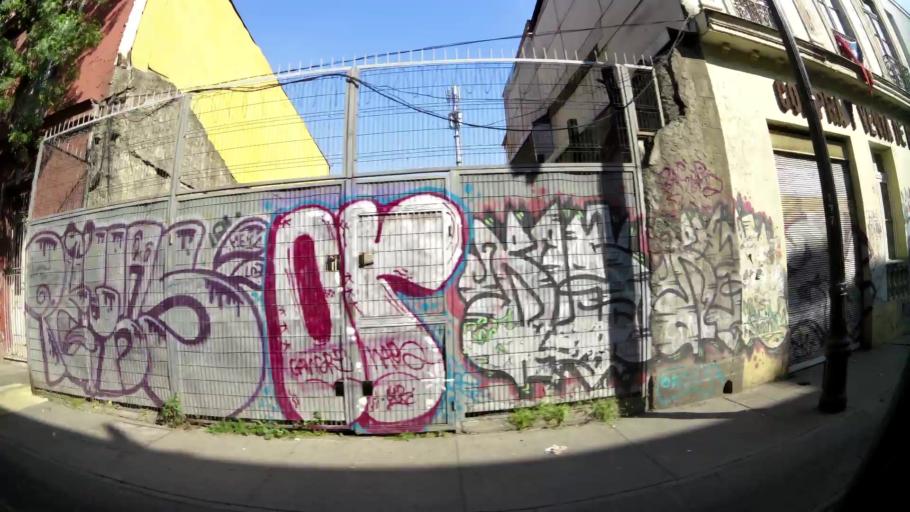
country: CL
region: Santiago Metropolitan
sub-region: Provincia de Santiago
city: Santiago
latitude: -33.4415
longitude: -70.6678
